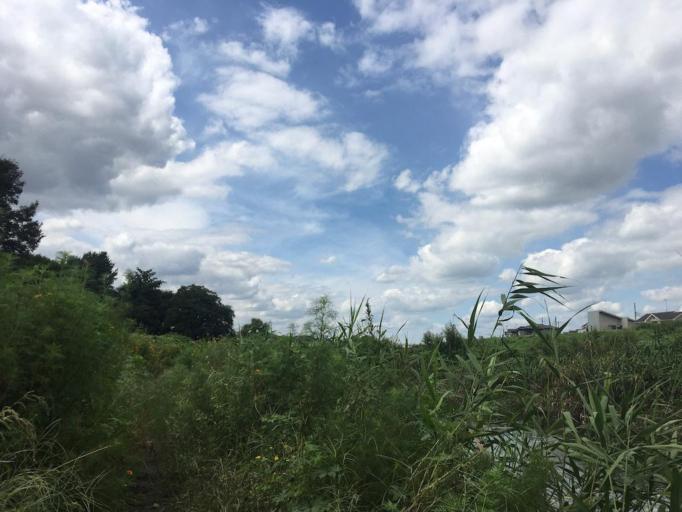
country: JP
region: Saitama
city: Kamifukuoka
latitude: 35.8905
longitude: 139.5071
